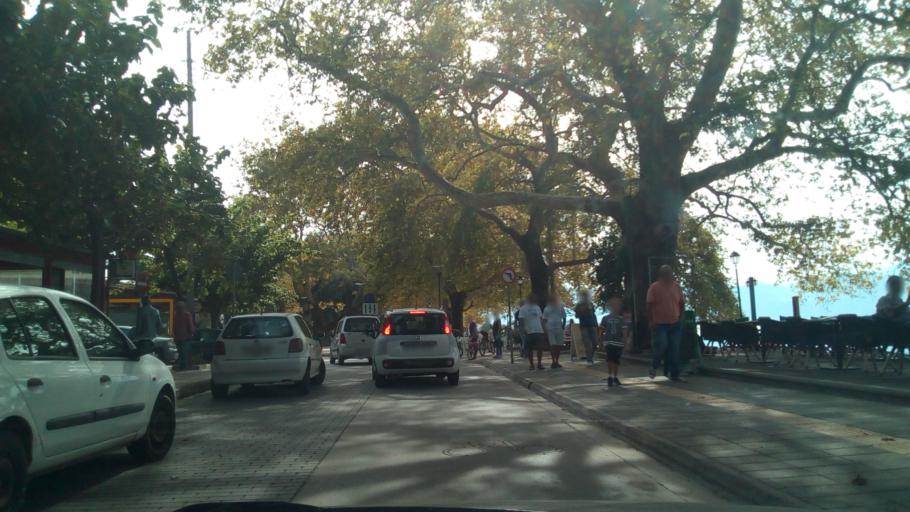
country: GR
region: West Greece
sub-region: Nomos Aitolias kai Akarnanias
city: Nafpaktos
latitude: 38.3907
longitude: 21.8393
